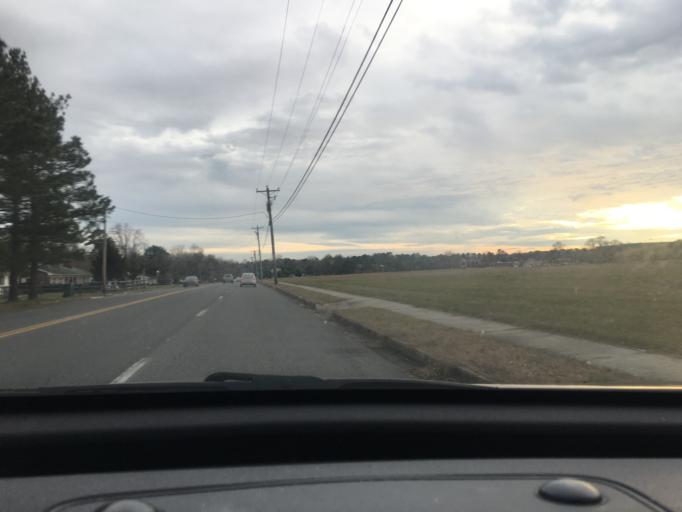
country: US
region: Maryland
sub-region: Wicomico County
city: Salisbury
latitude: 38.3646
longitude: -75.5676
